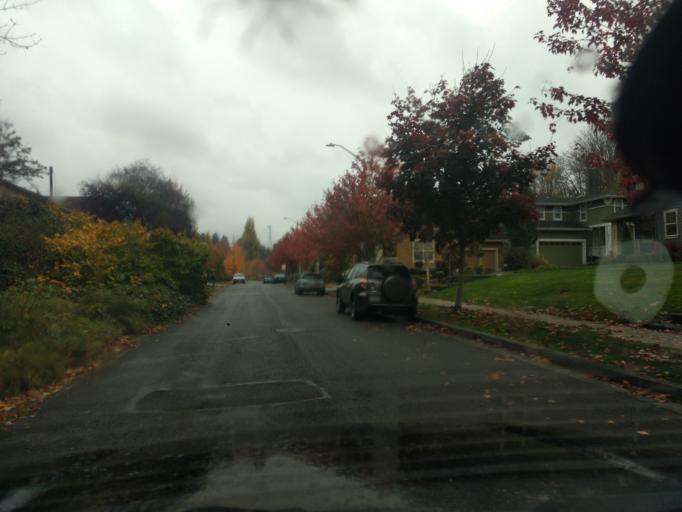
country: US
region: Washington
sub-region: King County
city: Riverton
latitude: 47.5416
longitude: -122.2863
